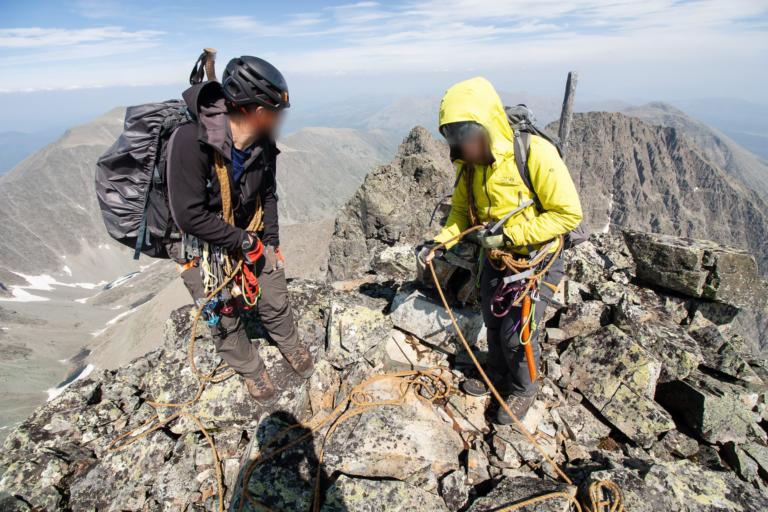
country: RU
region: Respublika Buryatiya
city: Kichera
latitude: 56.3741
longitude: 110.0757
